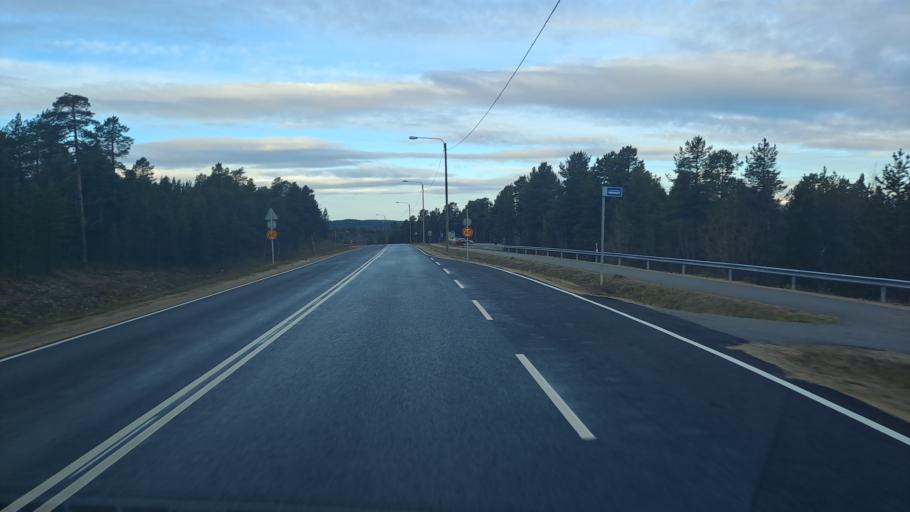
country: FI
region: Lapland
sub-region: Pohjois-Lappi
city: Inari
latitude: 68.9008
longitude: 27.0740
